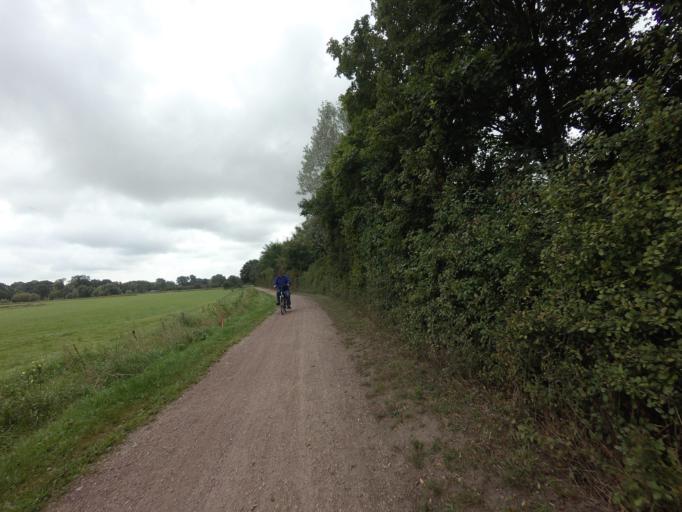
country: NL
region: Overijssel
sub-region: Gemeente Losser
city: Losser
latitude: 52.2613
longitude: 7.0155
